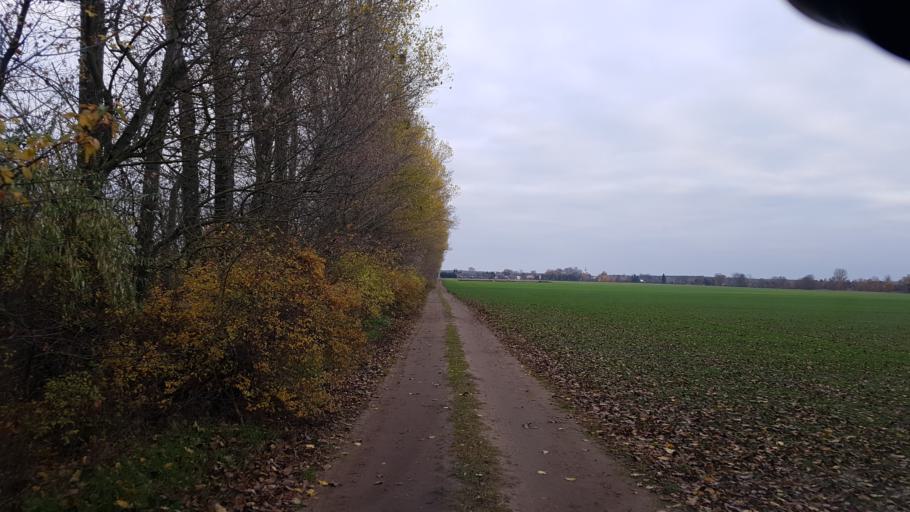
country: DE
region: Brandenburg
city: Sallgast
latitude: 51.6150
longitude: 13.8756
